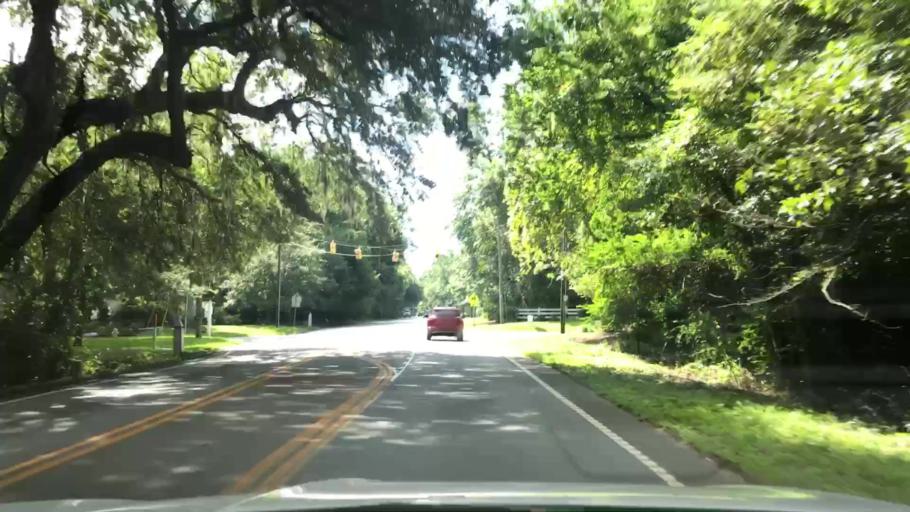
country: US
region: South Carolina
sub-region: Charleston County
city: Shell Point
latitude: 32.8563
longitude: -80.0731
